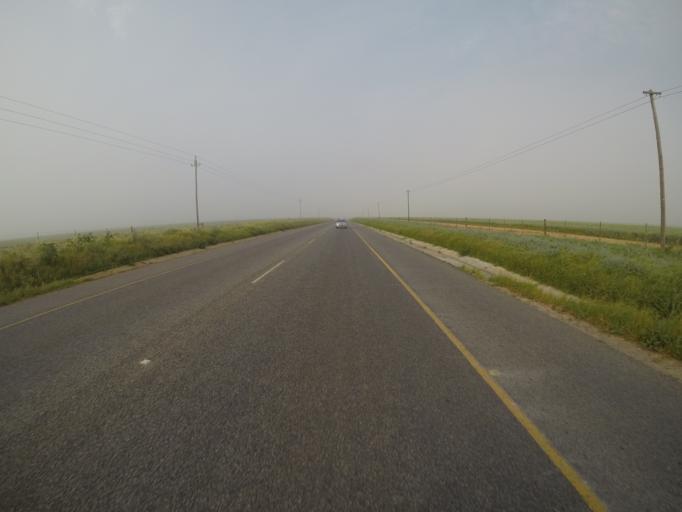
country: ZA
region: Western Cape
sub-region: West Coast District Municipality
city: Malmesbury
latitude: -33.6395
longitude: 18.7170
